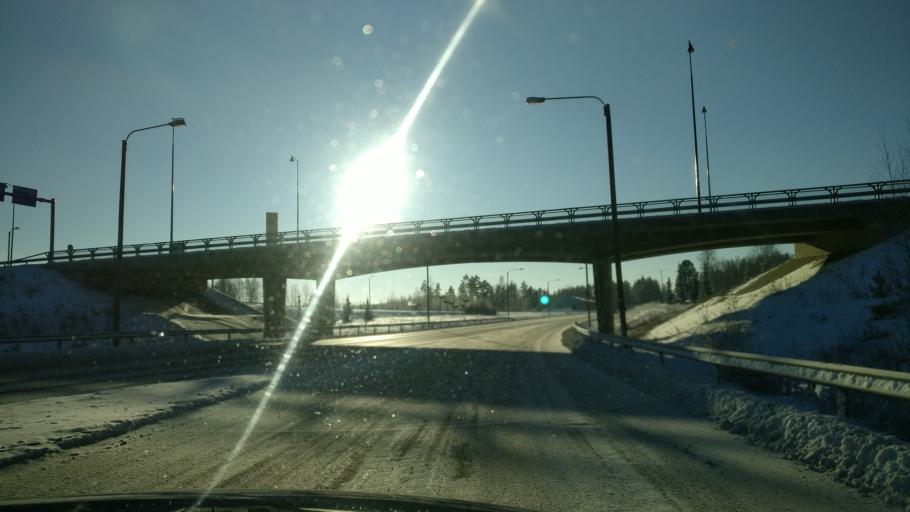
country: FI
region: Southern Savonia
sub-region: Pieksaemaeki
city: Juva
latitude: 61.8994
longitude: 27.8032
